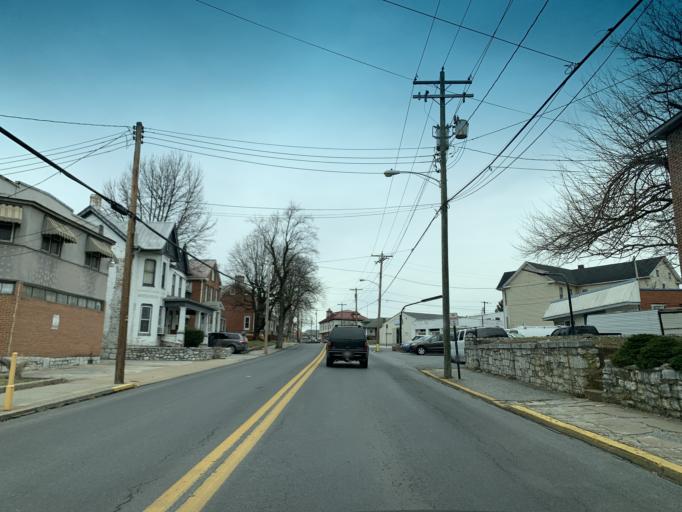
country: US
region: West Virginia
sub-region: Berkeley County
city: Martinsburg
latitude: 39.4648
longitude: -77.9596
